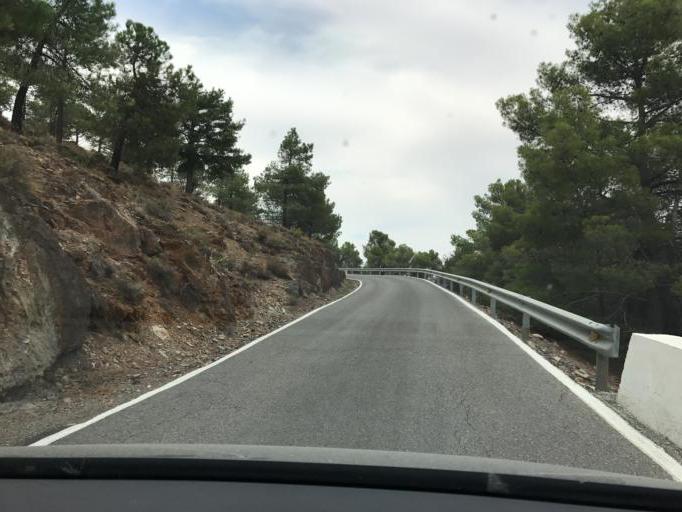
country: ES
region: Andalusia
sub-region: Provincia de Granada
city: Ferreira
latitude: 37.1633
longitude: -3.0501
